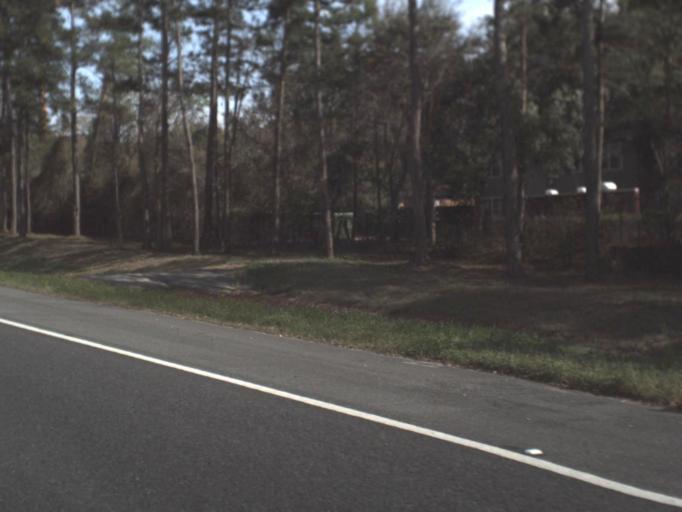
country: US
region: Florida
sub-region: Leon County
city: Tallahassee
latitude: 30.5017
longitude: -84.2460
